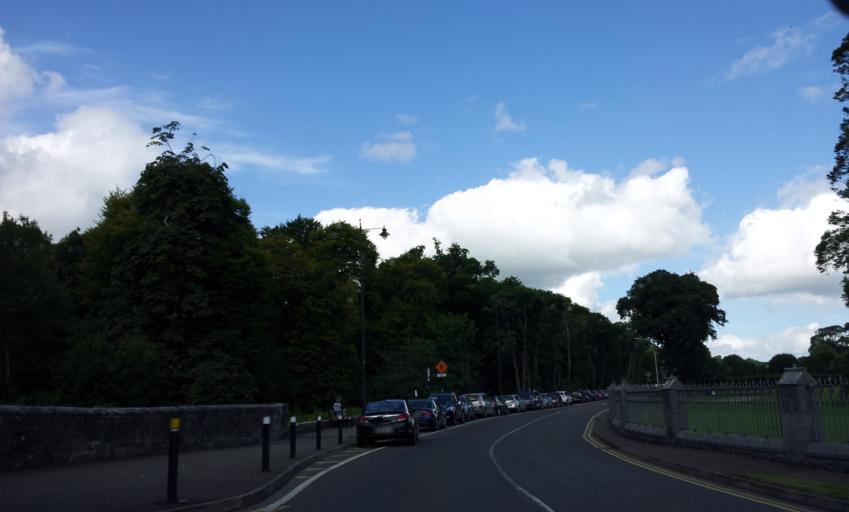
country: IE
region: Munster
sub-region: Ciarrai
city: Cill Airne
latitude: 52.0590
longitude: -9.5189
